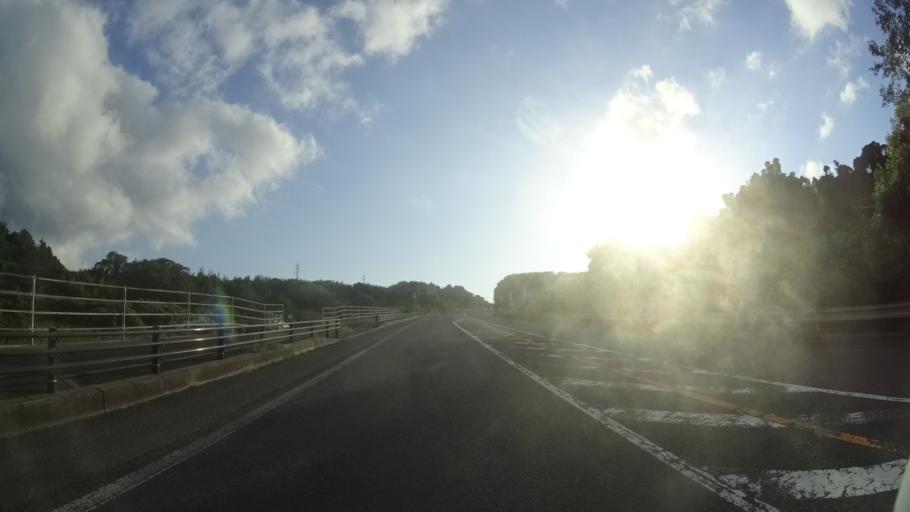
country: JP
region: Tottori
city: Yonago
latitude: 35.5176
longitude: 133.5525
